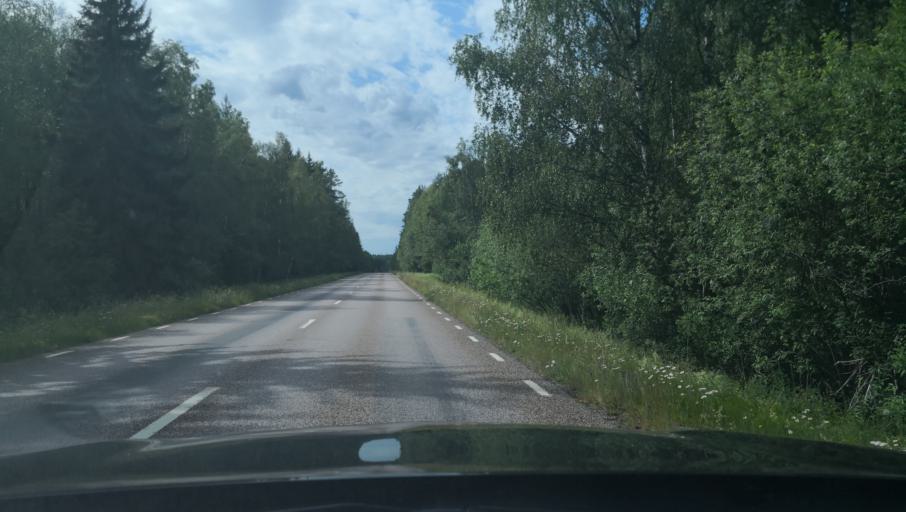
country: SE
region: Dalarna
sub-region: Avesta Kommun
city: Avesta
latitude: 59.9701
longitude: 16.1651
